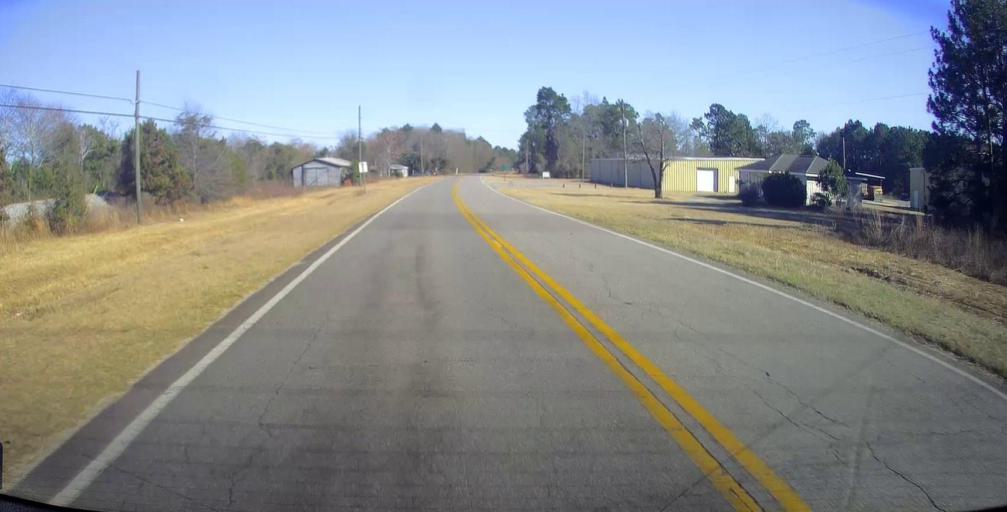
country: US
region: Georgia
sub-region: Taylor County
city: Butler
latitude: 32.5628
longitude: -84.2543
